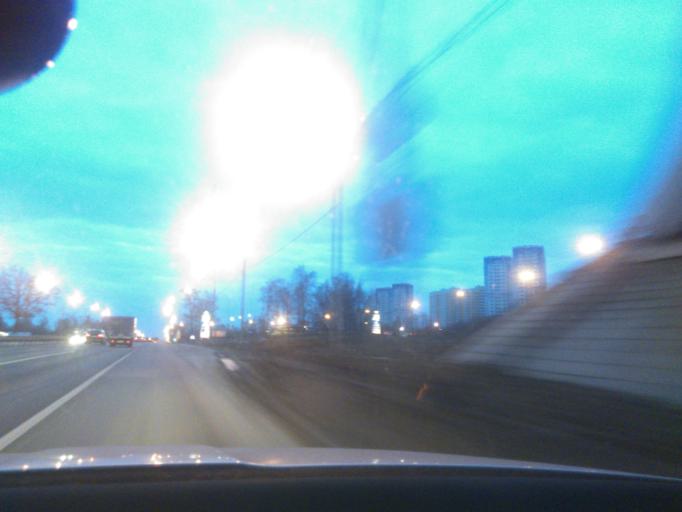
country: RU
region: Moskovskaya
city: Novopodrezkovo
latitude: 55.9538
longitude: 37.3454
